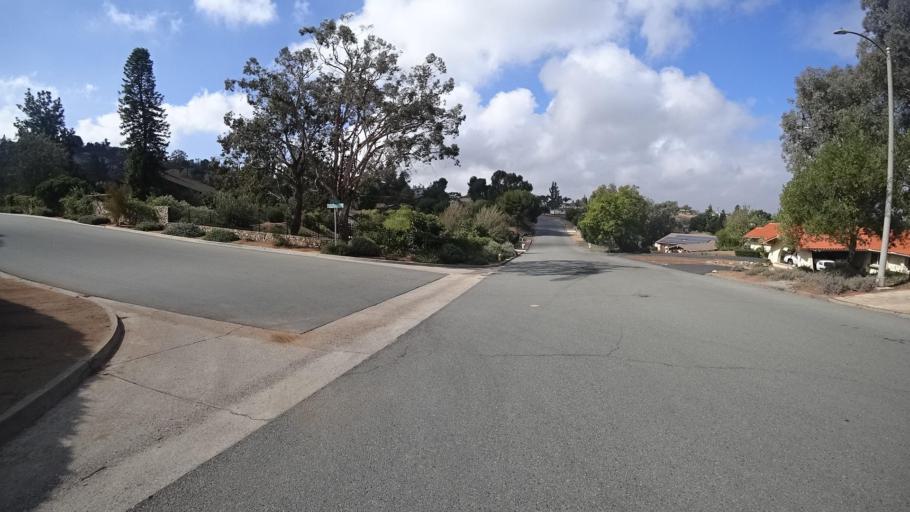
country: US
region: California
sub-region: San Diego County
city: Granite Hills
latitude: 32.7796
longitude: -116.8954
